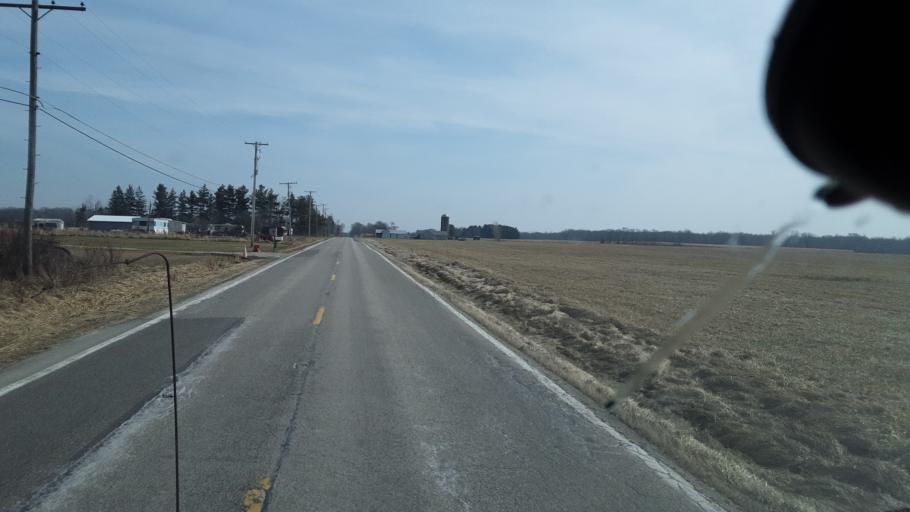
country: US
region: Ohio
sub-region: Ashtabula County
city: Jefferson
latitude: 41.7519
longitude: -80.6496
